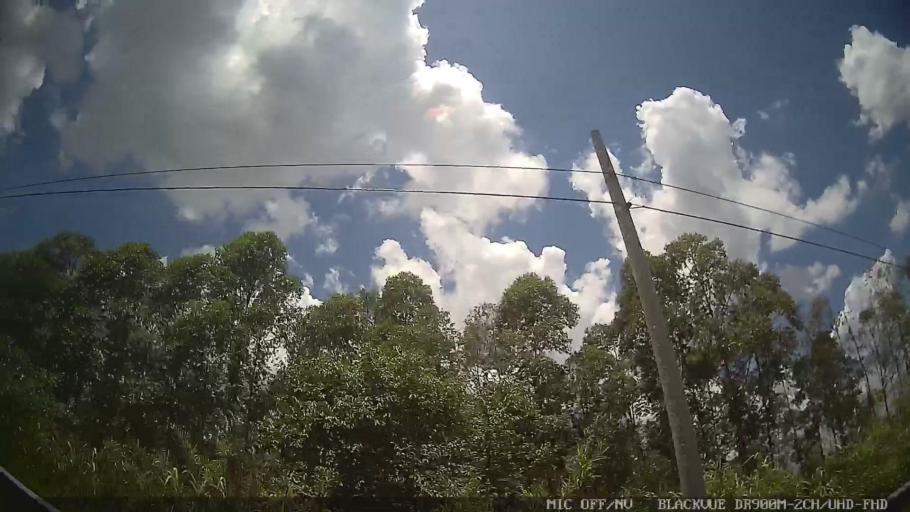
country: BR
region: Sao Paulo
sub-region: Amparo
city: Amparo
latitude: -22.6529
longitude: -46.7431
